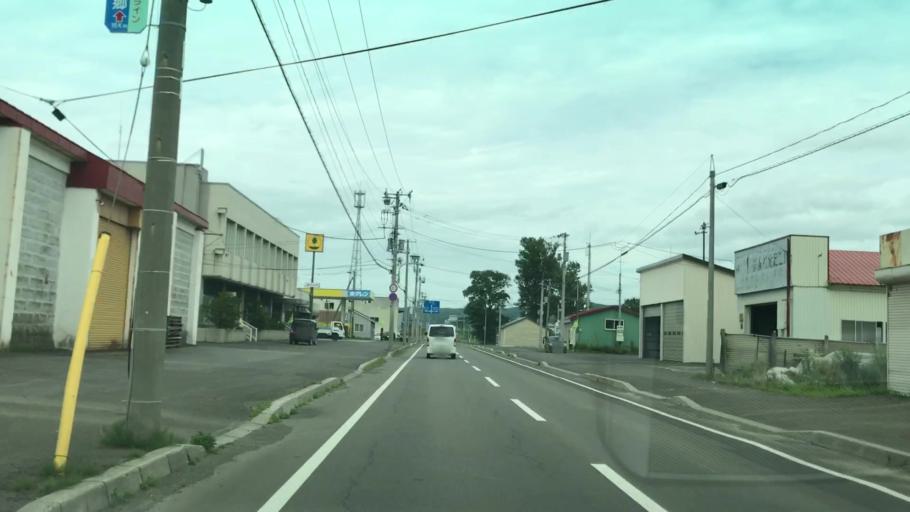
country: JP
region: Hokkaido
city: Iwanai
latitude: 43.0148
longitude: 140.5700
